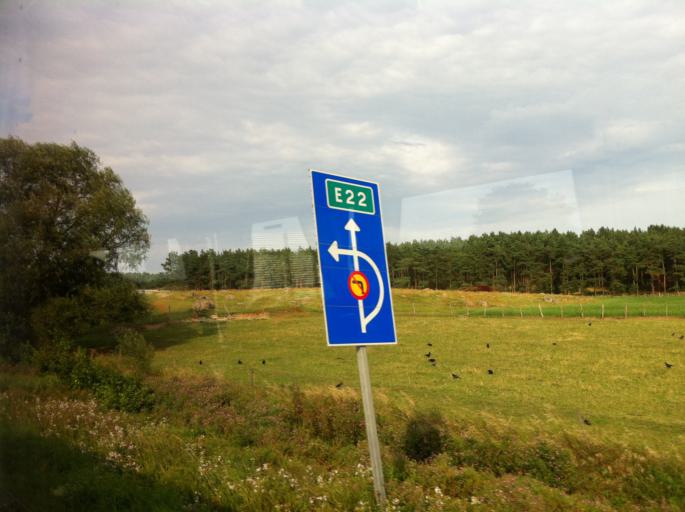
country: SE
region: Skane
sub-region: Kristianstads Kommun
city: Norra Asum
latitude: 55.9604
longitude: 14.0687
